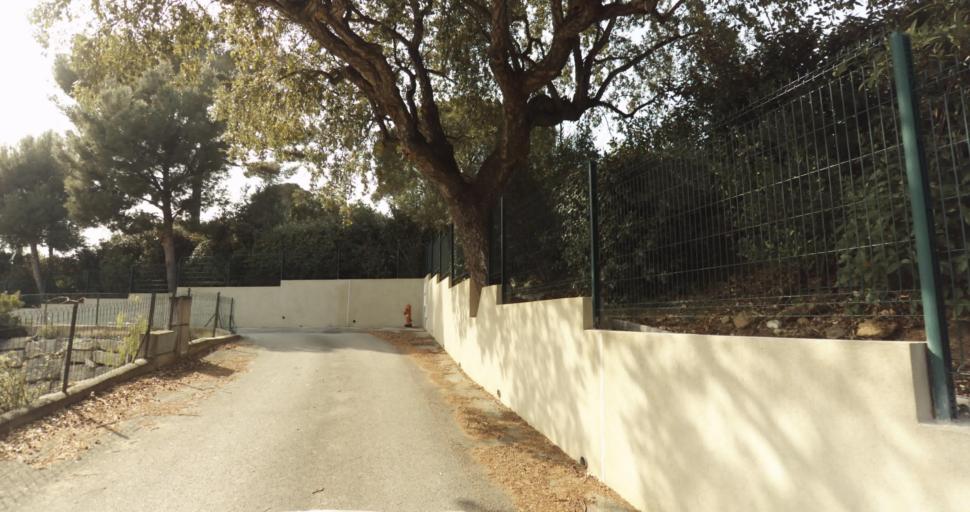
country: FR
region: Provence-Alpes-Cote d'Azur
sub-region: Departement du Var
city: Bormes-les-Mimosas
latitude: 43.1496
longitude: 6.3243
